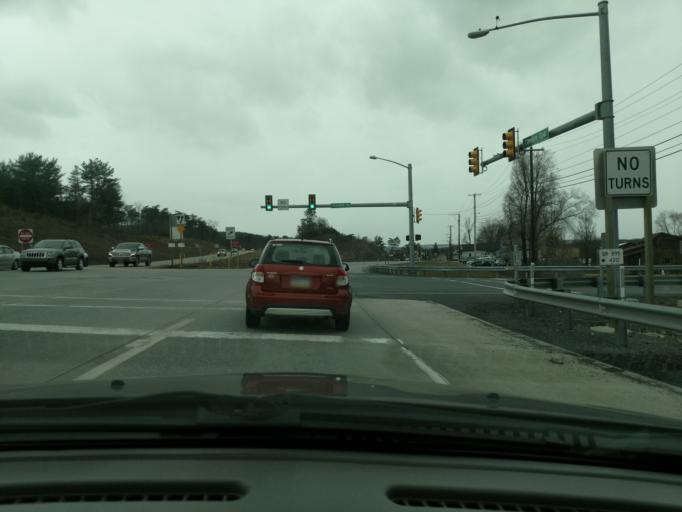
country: US
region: Pennsylvania
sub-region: Schuylkill County
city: Orwigsburg
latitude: 40.6197
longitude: -76.0581
